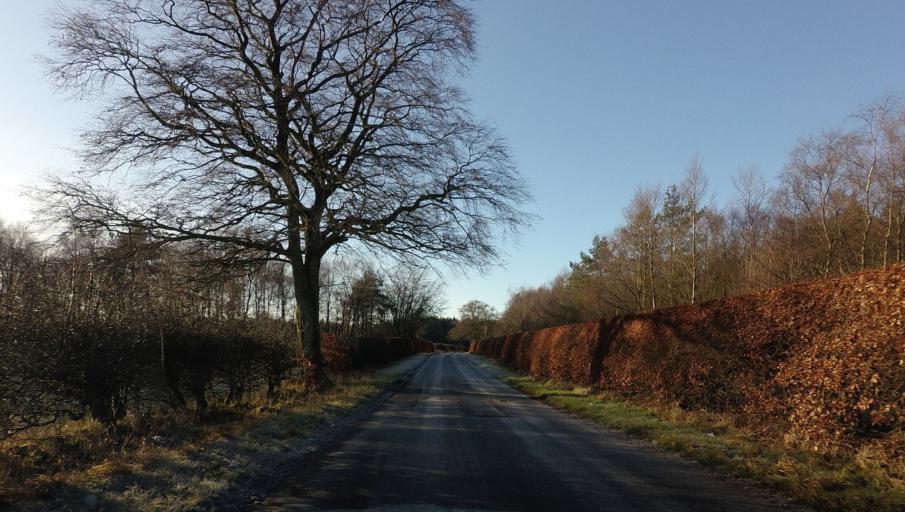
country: GB
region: Scotland
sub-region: North Lanarkshire
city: Newmains
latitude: 55.8063
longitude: -3.8658
